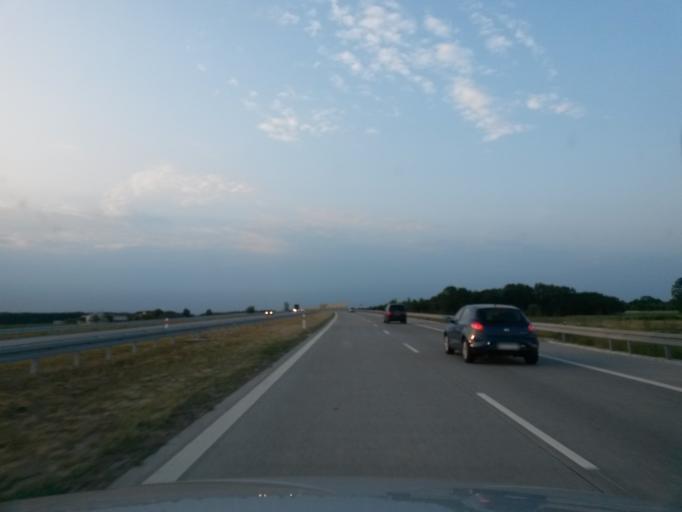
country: PL
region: Lodz Voivodeship
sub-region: Powiat sieradzki
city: Zloczew
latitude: 51.4154
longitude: 18.6411
